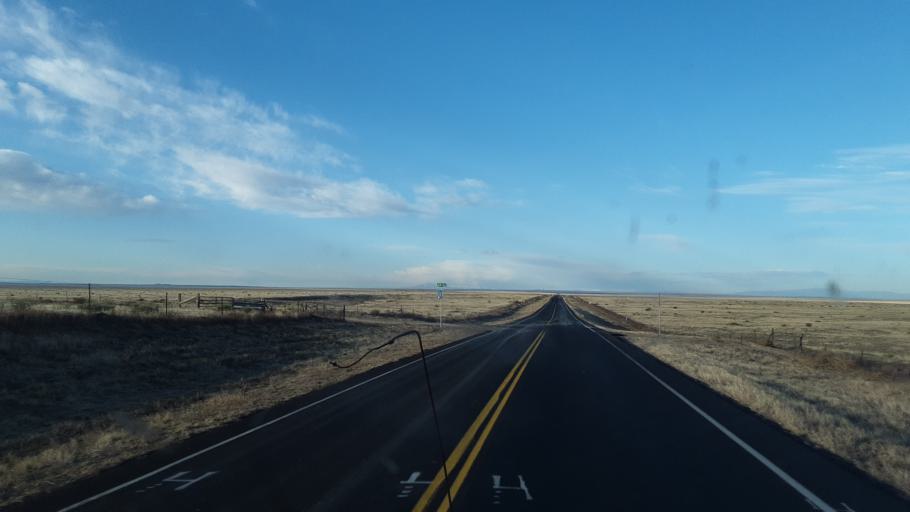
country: US
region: Colorado
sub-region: Otero County
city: Rocky Ford
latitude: 37.9703
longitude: -103.8202
